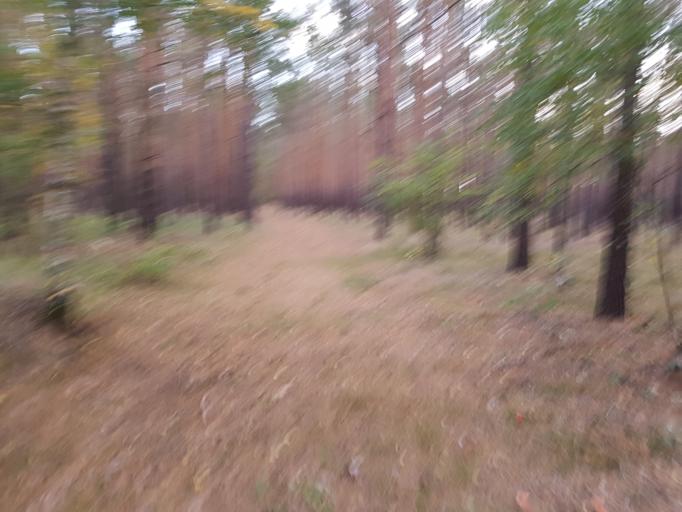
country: DE
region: Brandenburg
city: Schilda
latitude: 51.6014
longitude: 13.3855
